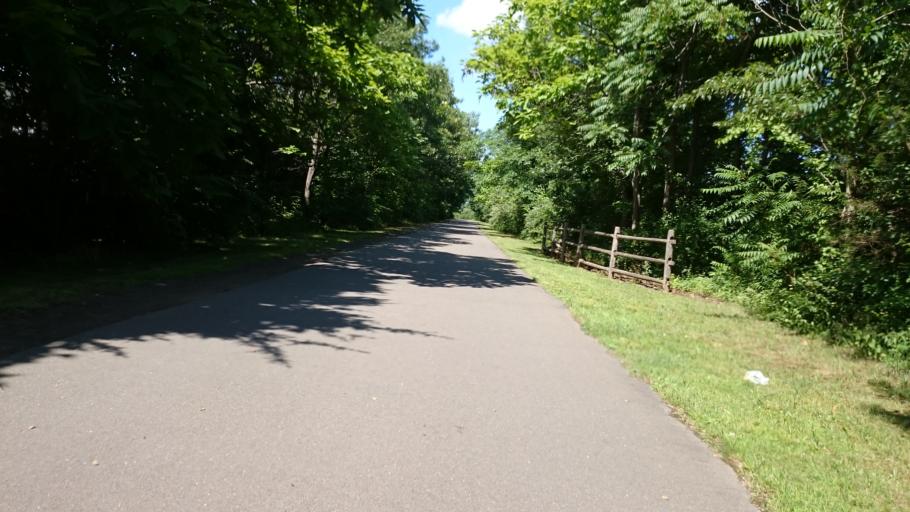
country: US
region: Connecticut
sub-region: New Haven County
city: Hamden
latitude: 41.3683
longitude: -72.9176
